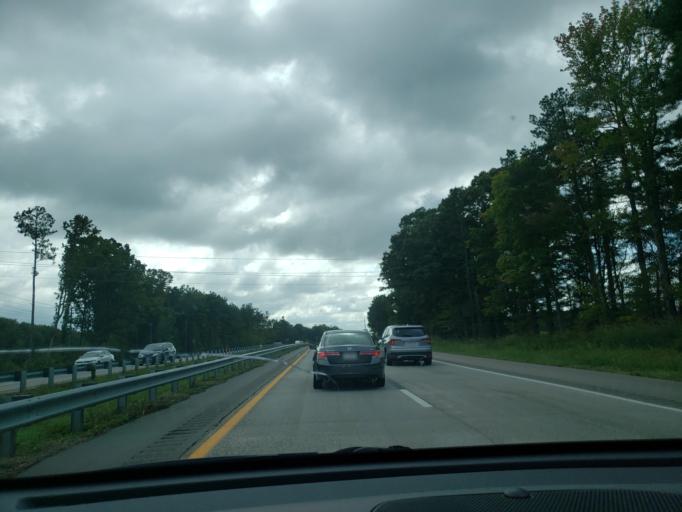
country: US
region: North Carolina
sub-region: Vance County
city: Henderson
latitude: 36.3861
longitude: -78.3448
